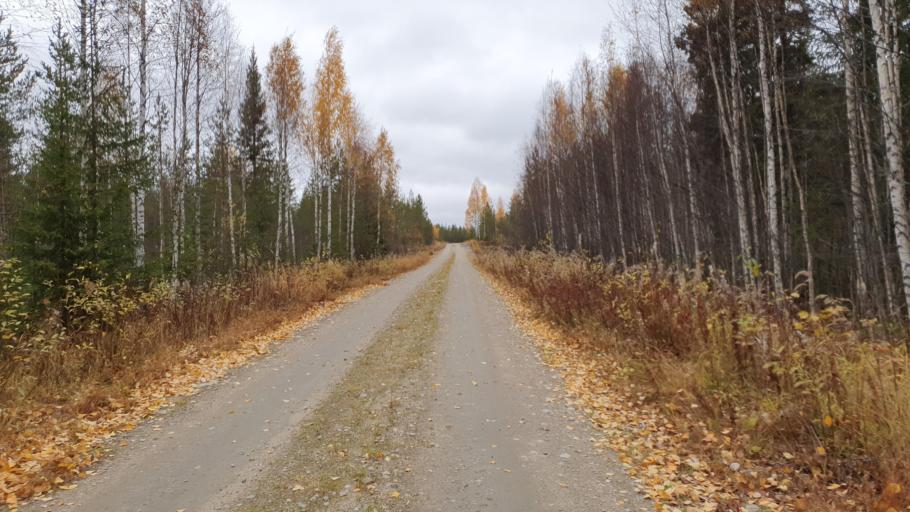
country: FI
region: Kainuu
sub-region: Kehys-Kainuu
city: Kuhmo
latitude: 64.4532
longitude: 29.6080
